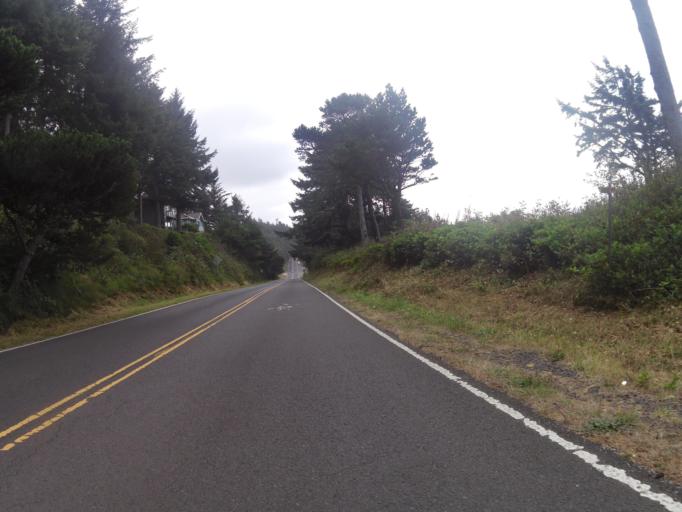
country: US
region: Oregon
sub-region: Lincoln County
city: Newport
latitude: 44.6610
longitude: -124.0569
